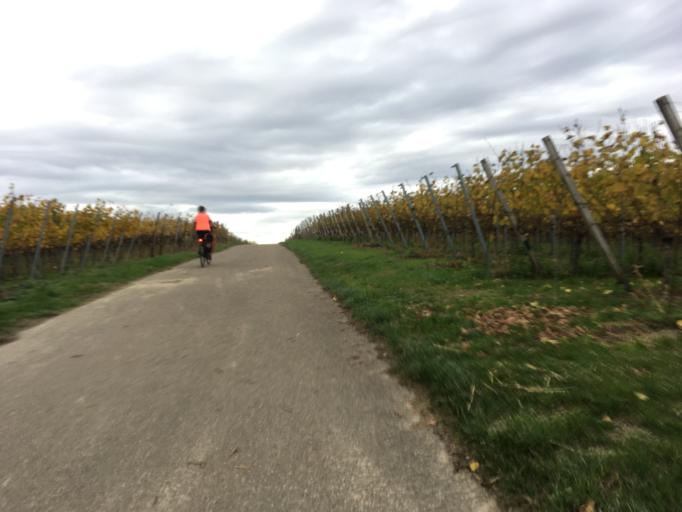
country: DE
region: Baden-Wuerttemberg
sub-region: Freiburg Region
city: Merdingen
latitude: 48.0219
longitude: 7.7033
